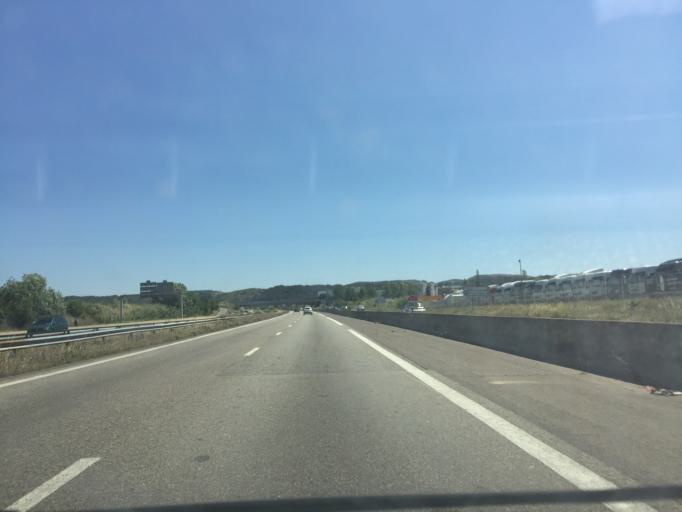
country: FR
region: Provence-Alpes-Cote d'Azur
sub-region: Departement des Bouches-du-Rhone
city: Saint-Victoret
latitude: 43.4250
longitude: 5.2647
